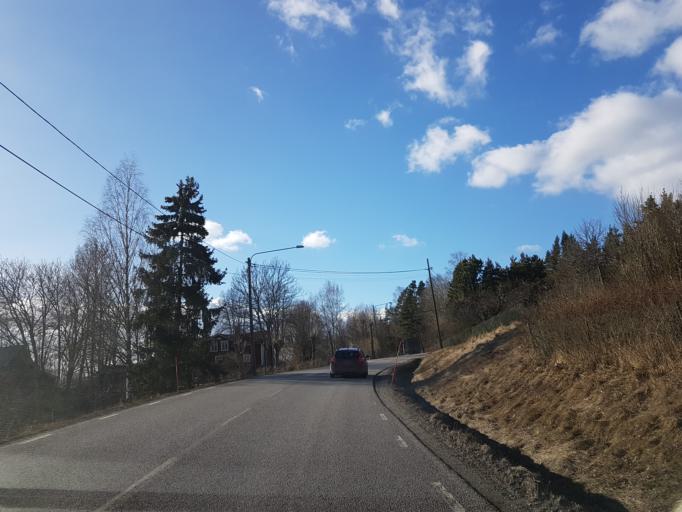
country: SE
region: Stockholm
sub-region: Norrtalje Kommun
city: Rimbo
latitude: 59.7344
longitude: 18.4129
